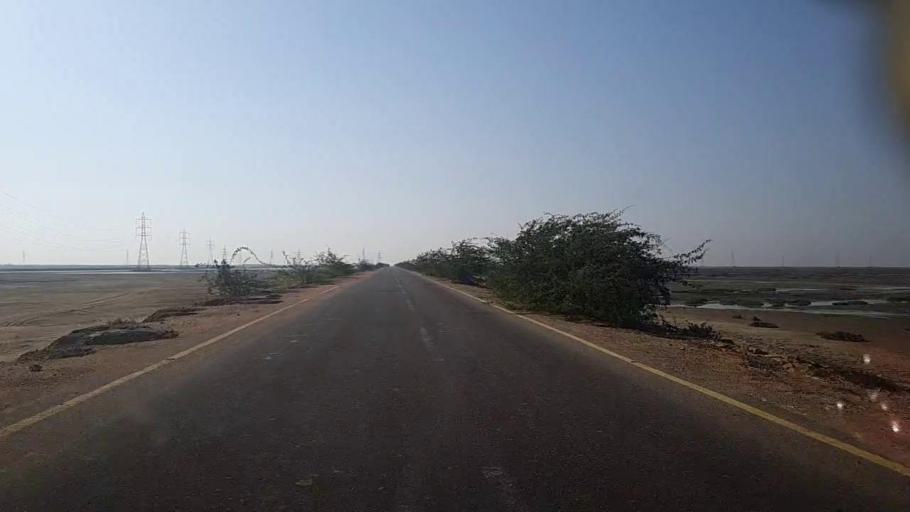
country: PK
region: Sindh
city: Mirpur Sakro
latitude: 24.5996
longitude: 67.4980
